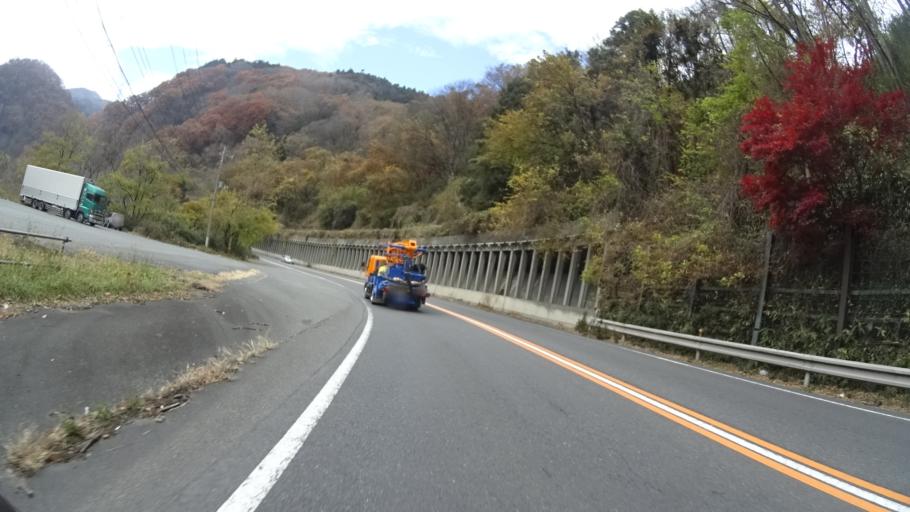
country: JP
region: Gunma
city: Numata
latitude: 36.5859
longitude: 139.0546
